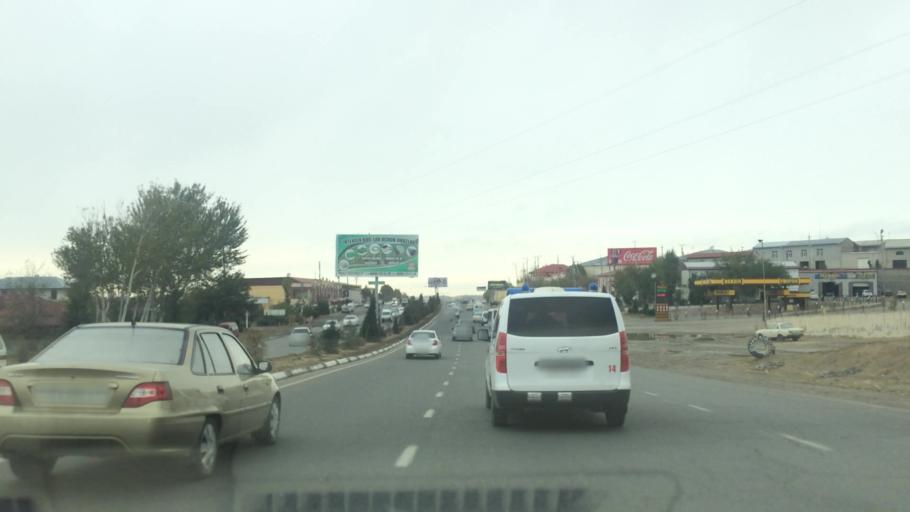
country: UZ
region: Samarqand
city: Samarqand
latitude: 39.6759
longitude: 67.0135
